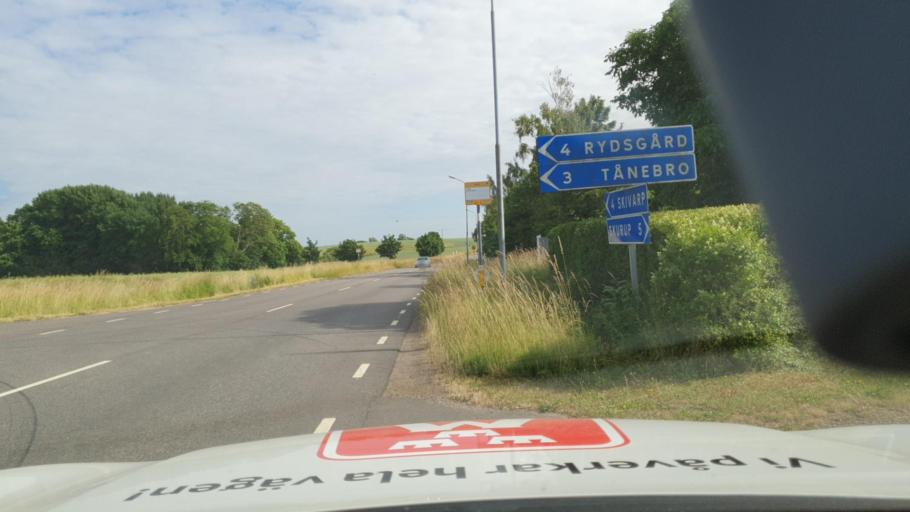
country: SE
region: Skane
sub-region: Skurups Kommun
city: Rydsgard
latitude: 55.4514
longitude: 13.5463
